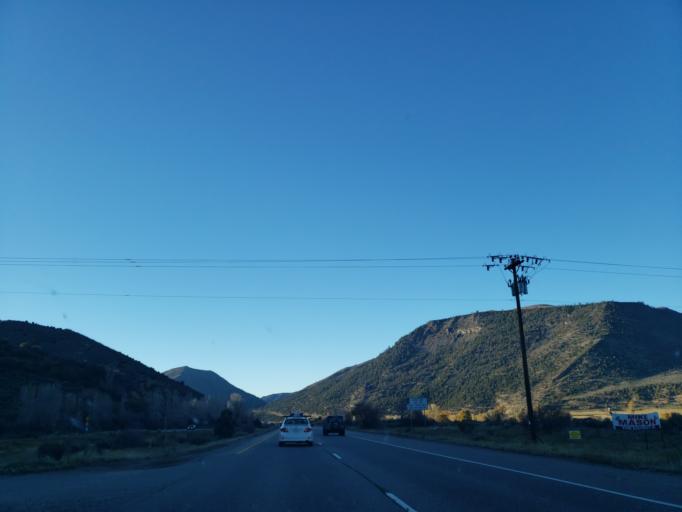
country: US
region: Colorado
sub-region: Pitkin County
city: Snowmass Village
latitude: 39.2819
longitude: -106.9005
